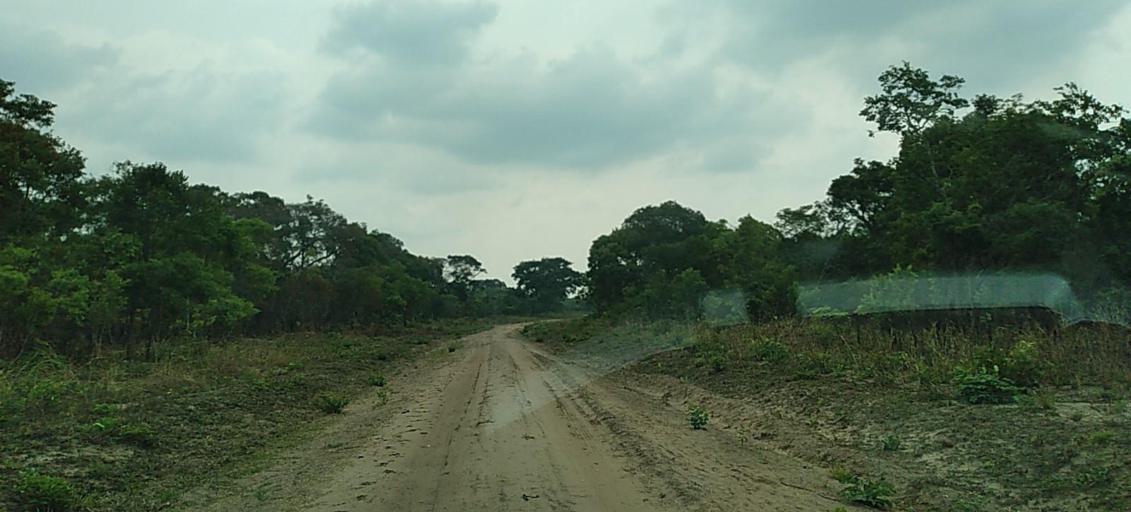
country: ZM
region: North-Western
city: Mwinilunga
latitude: -11.4141
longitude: 24.6108
